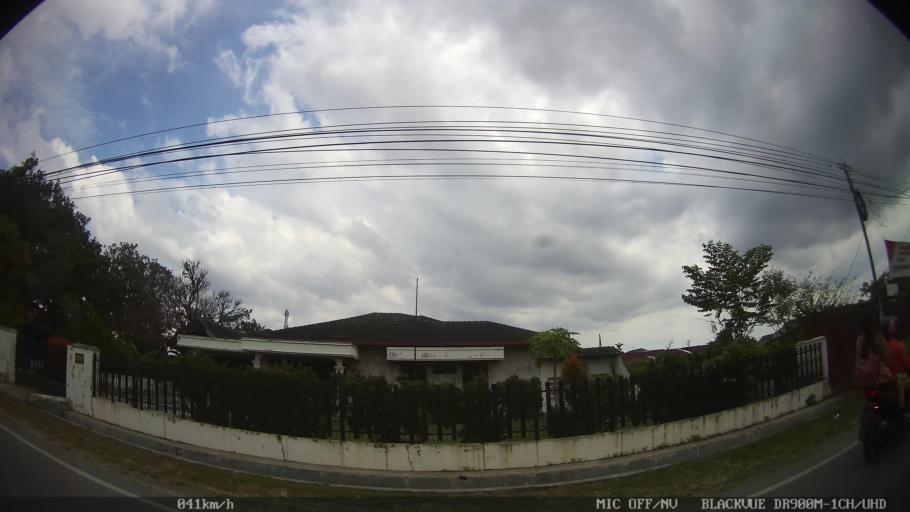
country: ID
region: North Sumatra
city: Sunggal
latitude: 3.6180
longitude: 98.6209
